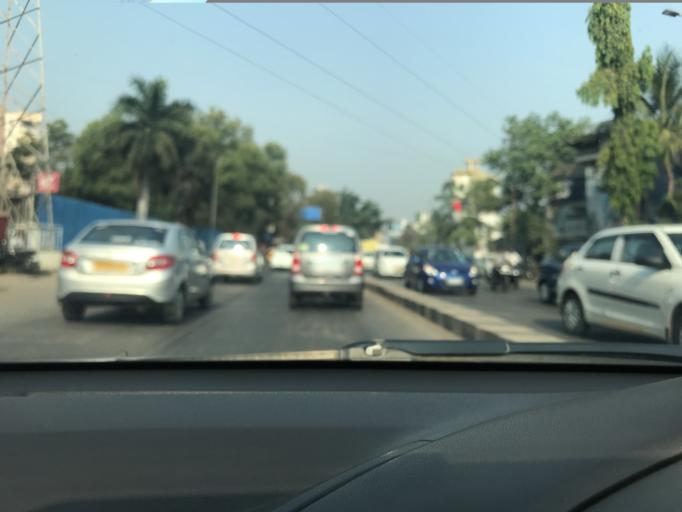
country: IN
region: Maharashtra
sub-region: Pune Division
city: Khadki
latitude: 18.5525
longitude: 73.8034
